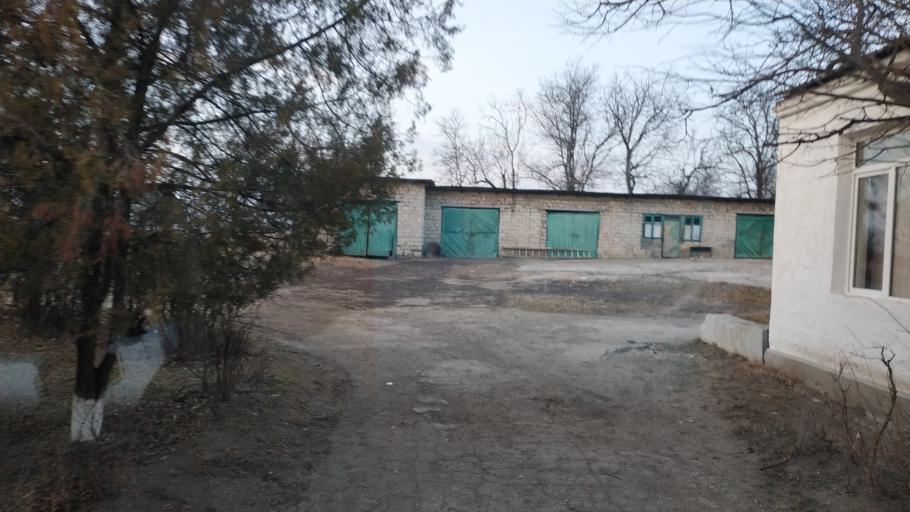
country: MD
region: Hincesti
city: Dancu
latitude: 46.6723
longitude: 28.3236
